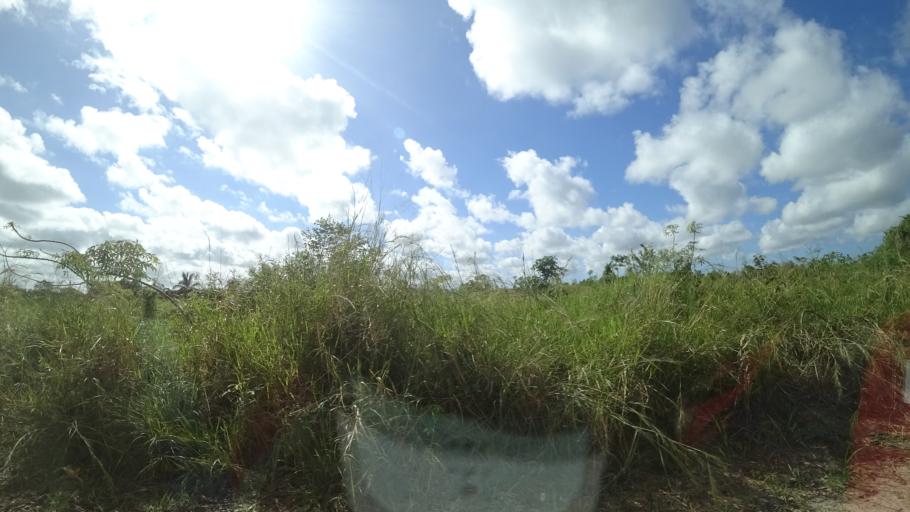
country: MZ
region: Sofala
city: Beira
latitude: -19.6211
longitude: 35.0606
